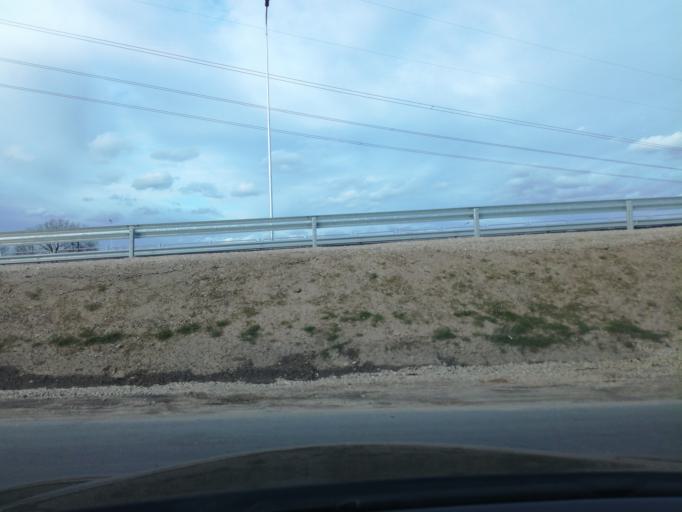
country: LT
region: Marijampoles apskritis
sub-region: Marijampole Municipality
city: Marijampole
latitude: 54.5956
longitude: 23.3911
